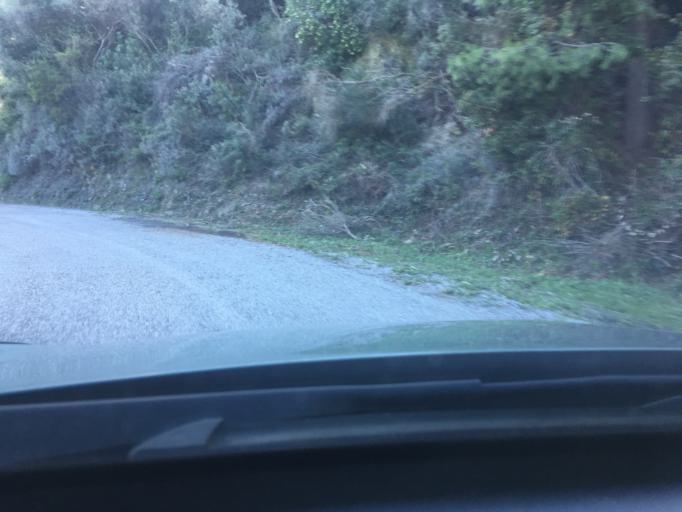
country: GR
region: Thessaly
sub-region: Nomos Magnisias
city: Skopelos
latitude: 39.1763
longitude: 23.6341
